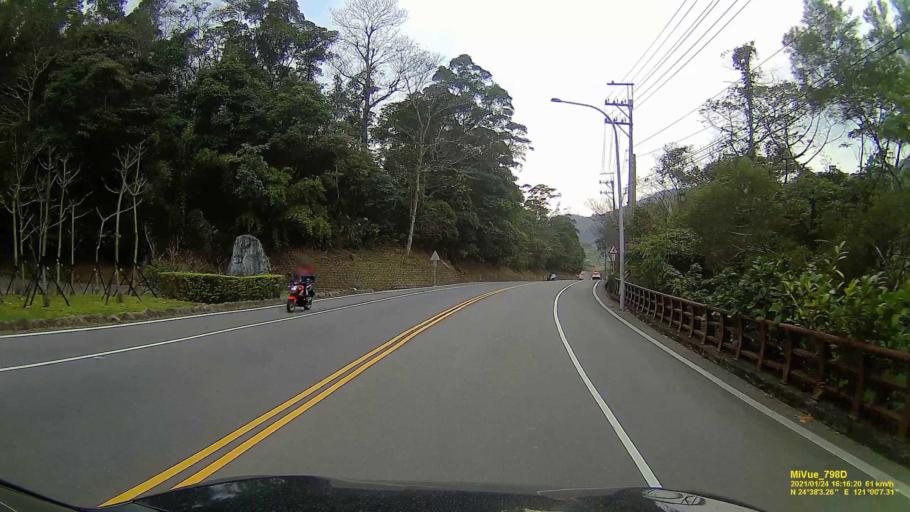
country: TW
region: Taiwan
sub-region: Hsinchu
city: Hsinchu
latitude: 24.6343
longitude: 121.0016
